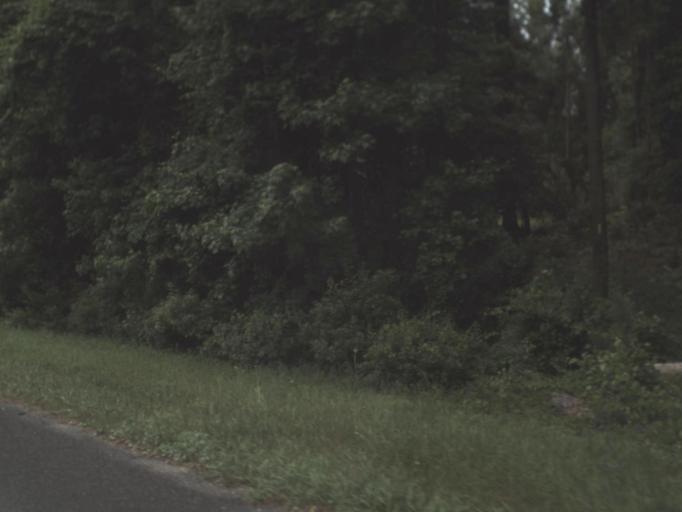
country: US
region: Georgia
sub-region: Charlton County
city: Folkston
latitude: 30.7653
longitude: -81.9697
